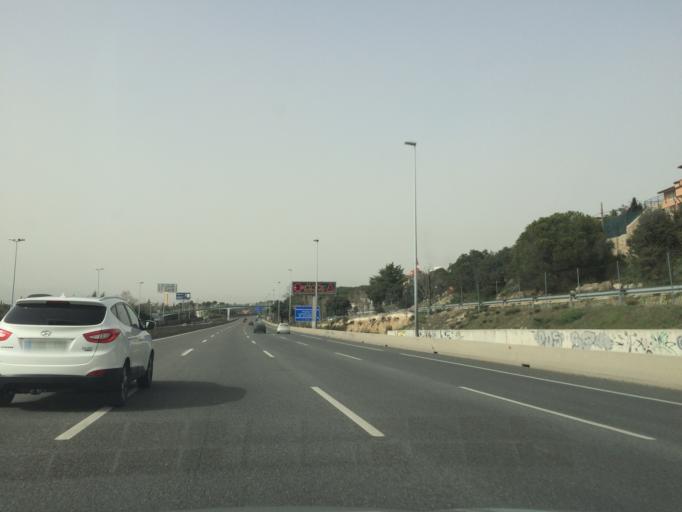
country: ES
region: Madrid
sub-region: Provincia de Madrid
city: Torrelodones
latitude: 40.5812
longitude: -3.9478
